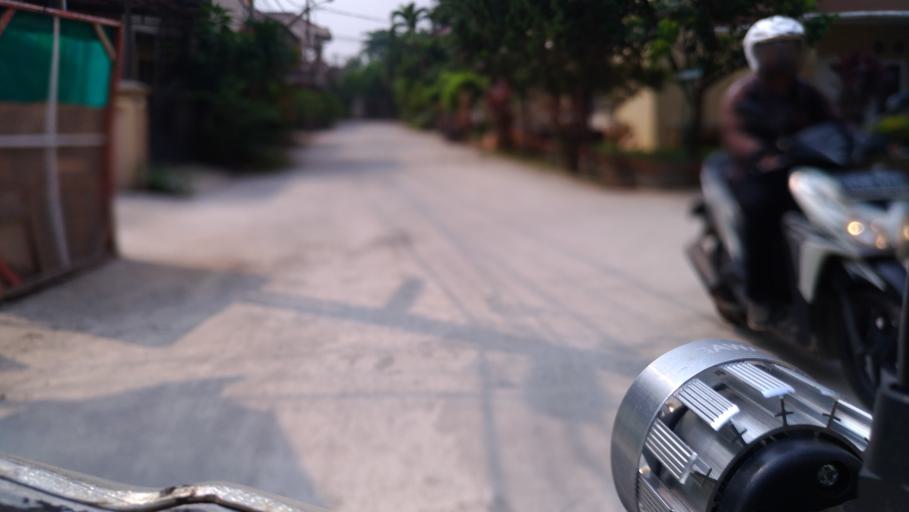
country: ID
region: West Java
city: Depok
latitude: -6.3680
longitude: 106.8774
